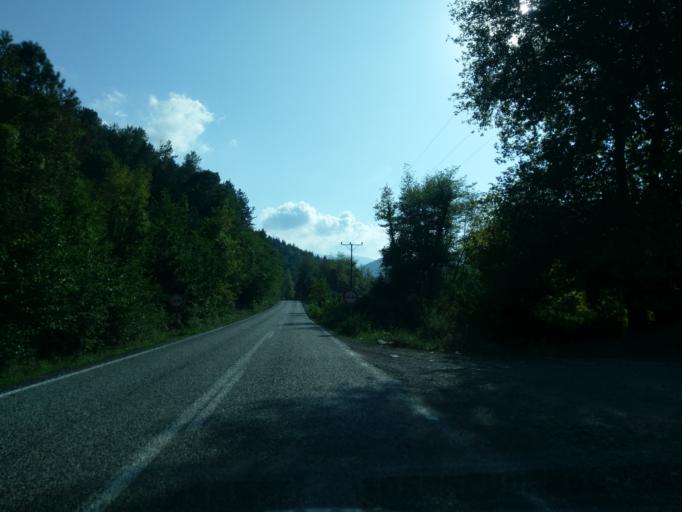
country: TR
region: Sinop
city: Yenikonak
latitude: 41.8848
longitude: 34.5653
